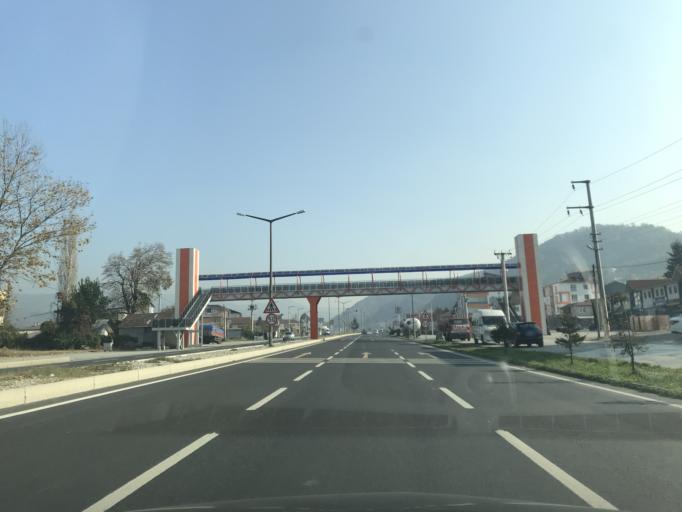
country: TR
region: Duzce
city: Kaynasli
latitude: 40.7742
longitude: 31.3148
